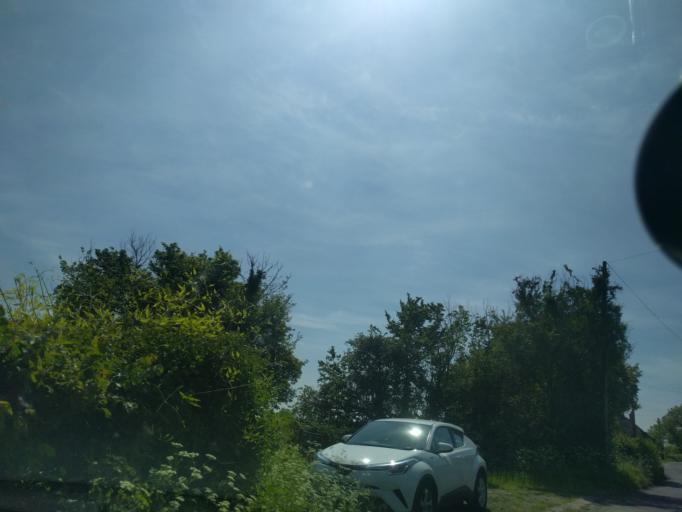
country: GB
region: England
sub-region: Somerset
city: Langport
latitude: 51.0811
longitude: -2.8178
